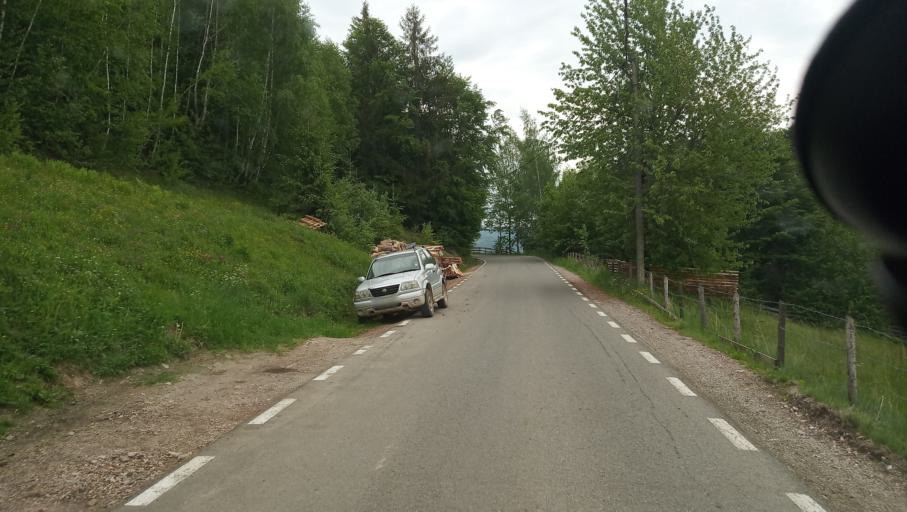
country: RO
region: Alba
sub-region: Comuna Horea
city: Horea
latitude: 46.5070
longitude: 22.9158
